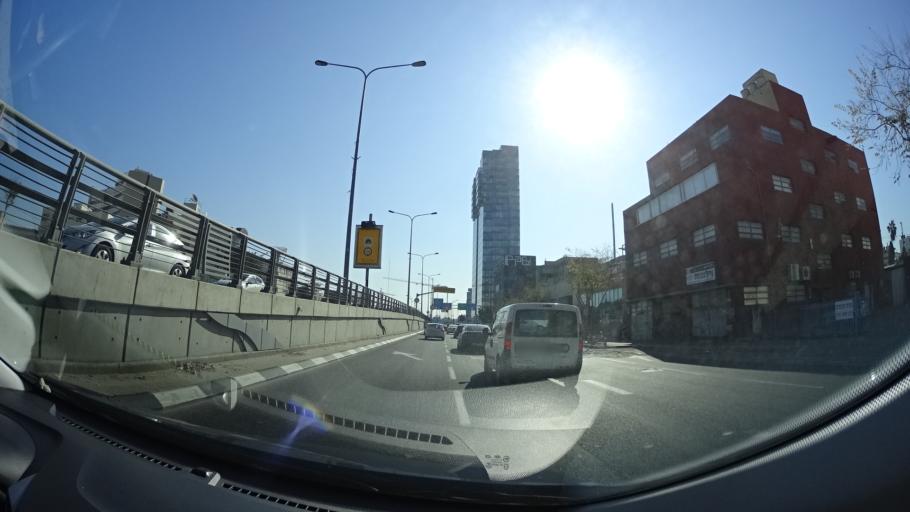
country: IL
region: Tel Aviv
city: Tel Aviv
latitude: 32.0619
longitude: 34.7807
